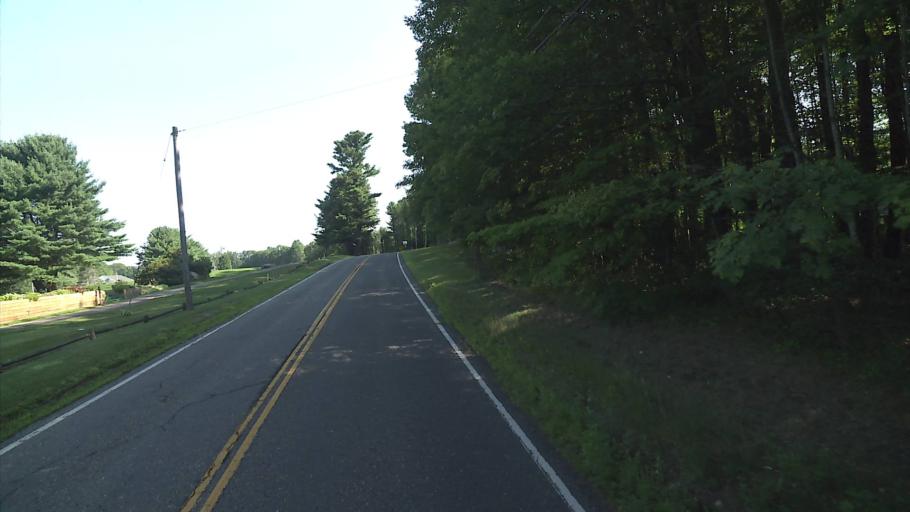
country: US
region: Connecticut
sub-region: Litchfield County
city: Winsted
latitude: 41.8831
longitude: -73.0652
